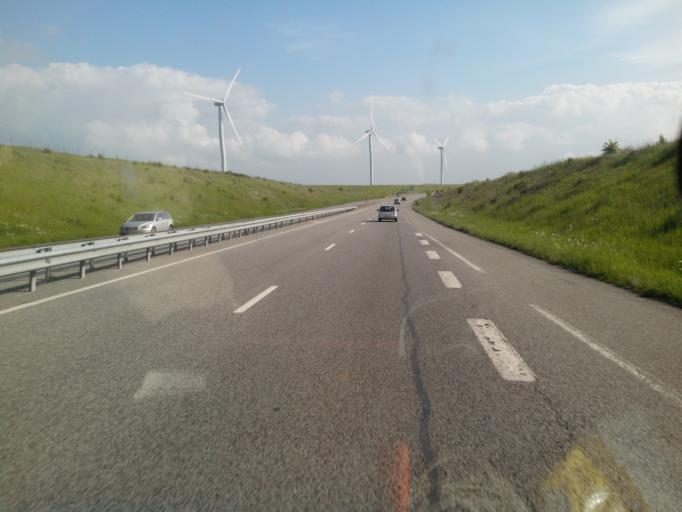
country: FR
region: Haute-Normandie
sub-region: Departement de la Seine-Maritime
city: Foucarmont
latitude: 49.8075
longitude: 1.5091
